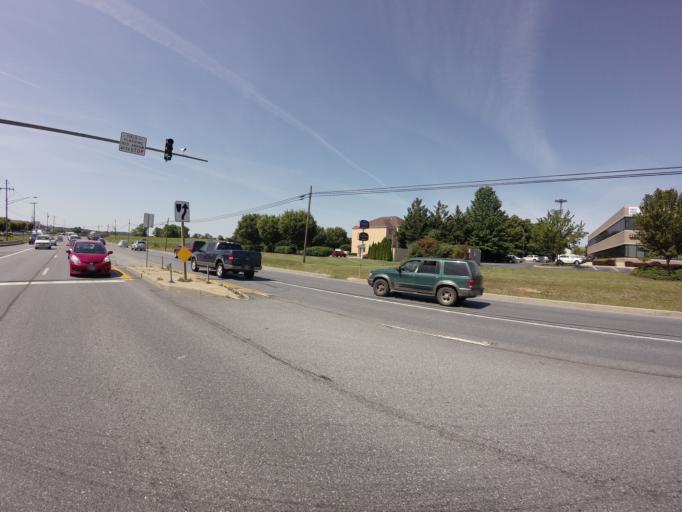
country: US
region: Maryland
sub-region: Frederick County
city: Ballenger Creek
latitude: 39.3794
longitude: -77.4095
